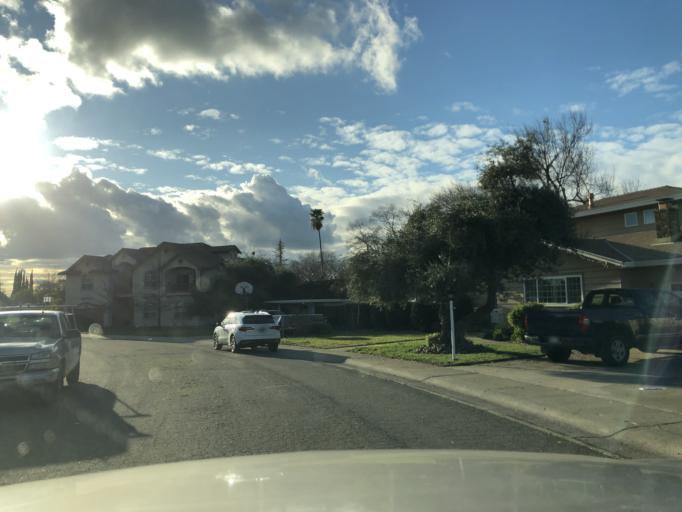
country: US
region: California
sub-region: Sacramento County
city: Fair Oaks
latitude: 38.6612
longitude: -121.3103
